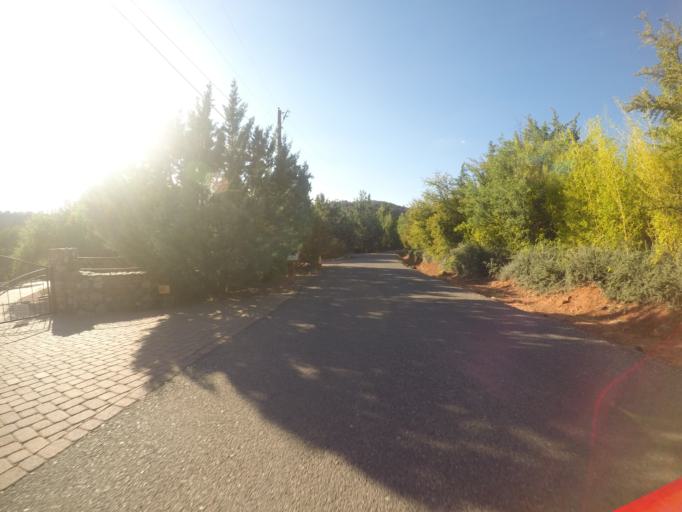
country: US
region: Arizona
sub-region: Yavapai County
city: West Sedona
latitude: 34.8296
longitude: -111.7944
